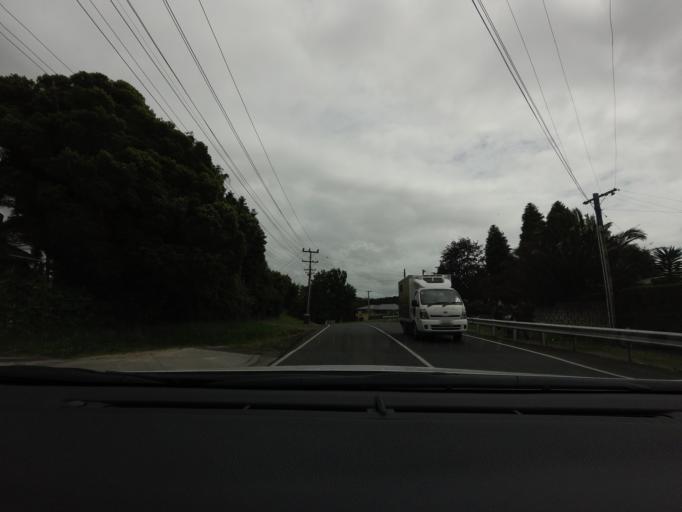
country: NZ
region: Auckland
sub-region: Auckland
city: Waitakere
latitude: -36.8967
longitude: 174.6104
